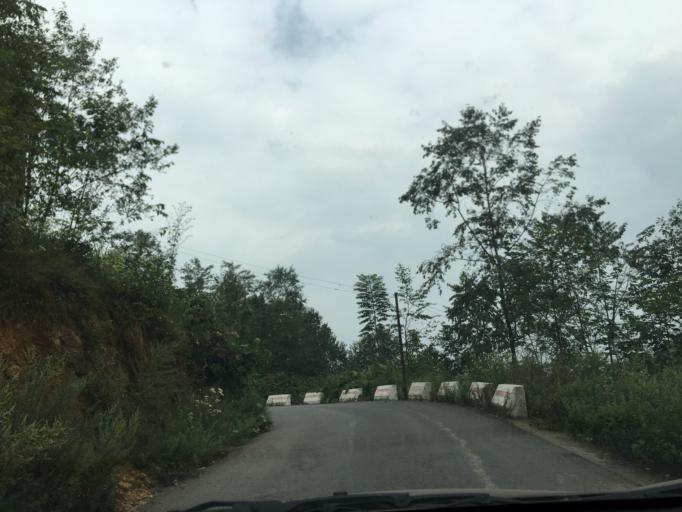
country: CN
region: Guangxi Zhuangzu Zizhiqu
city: Xinzhou
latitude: 25.5399
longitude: 105.5881
